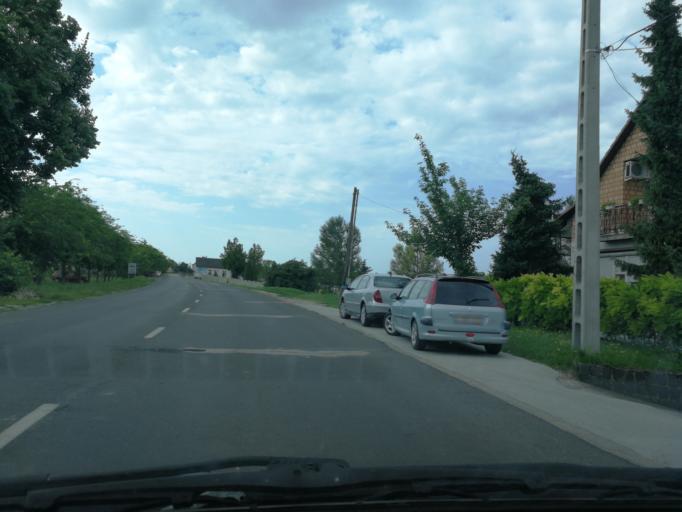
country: HU
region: Bacs-Kiskun
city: Baja
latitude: 46.2111
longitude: 18.9604
